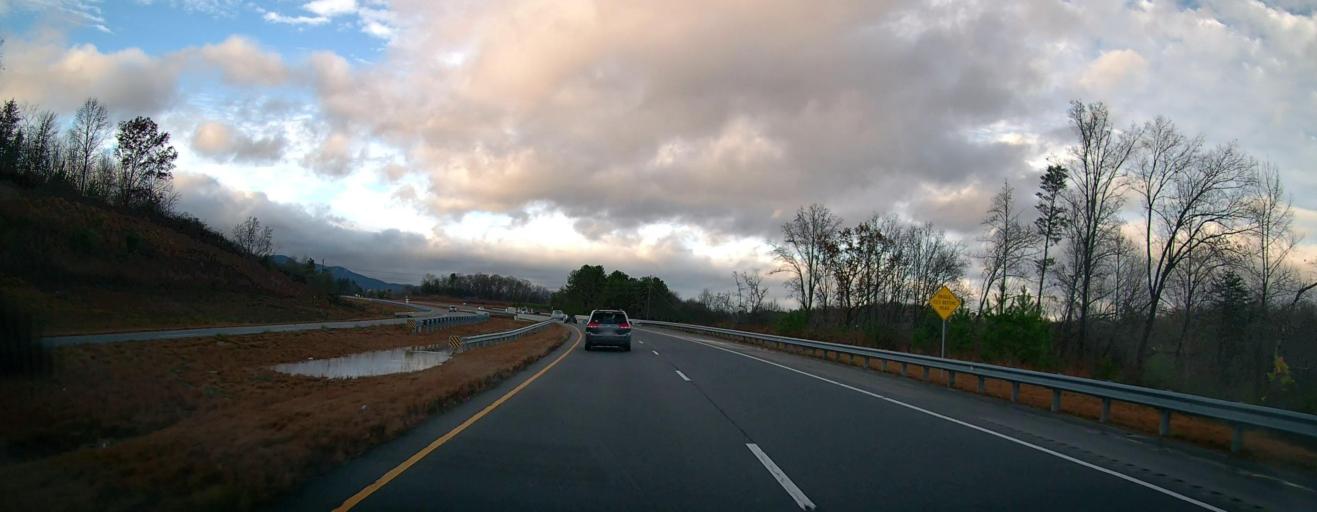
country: US
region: Georgia
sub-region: White County
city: Cleveland
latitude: 34.5982
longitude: -83.7807
